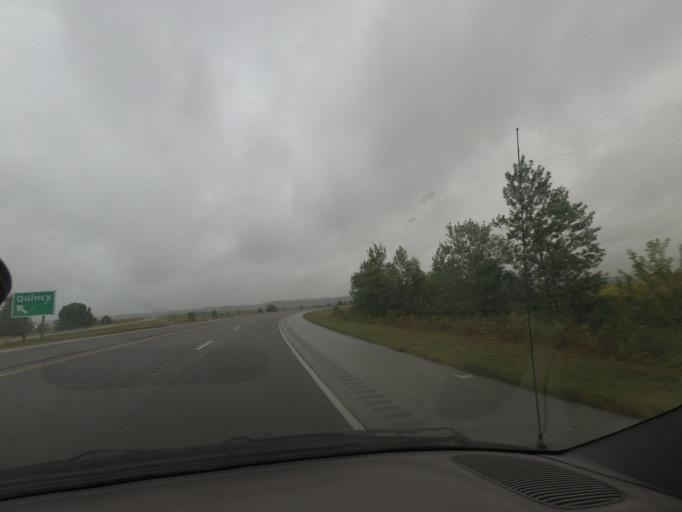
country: US
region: Missouri
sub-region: Marion County
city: Hannibal
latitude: 39.7504
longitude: -91.2999
